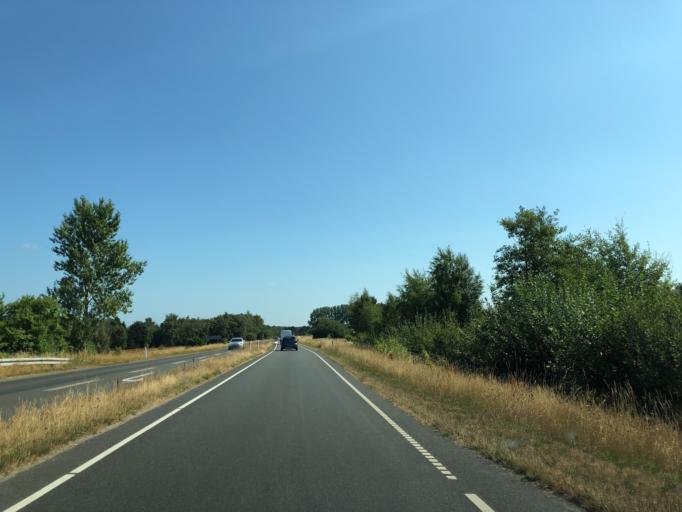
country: DK
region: Zealand
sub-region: Odsherred Kommune
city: Nykobing Sjaelland
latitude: 55.9306
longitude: 11.6591
